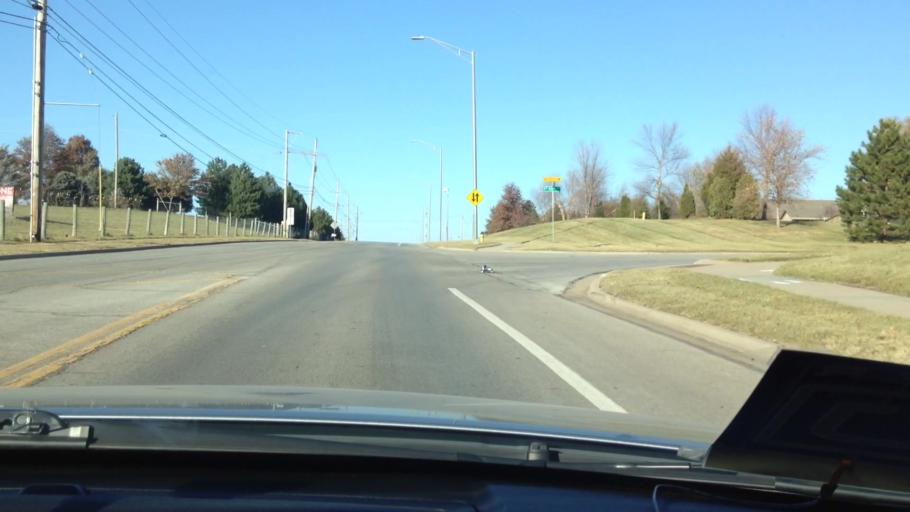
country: US
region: Kansas
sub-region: Johnson County
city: Olathe
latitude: 38.9286
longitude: -94.8160
